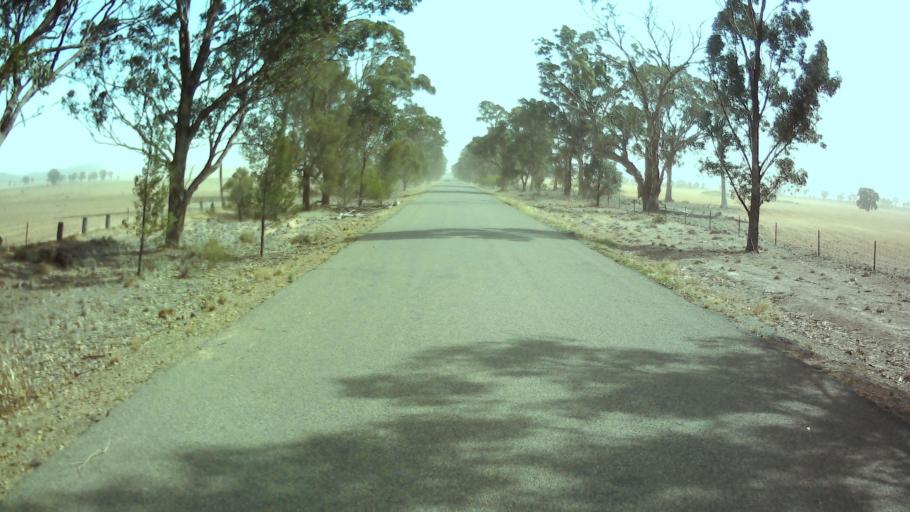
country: AU
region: New South Wales
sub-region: Weddin
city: Grenfell
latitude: -33.7606
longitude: 147.9889
